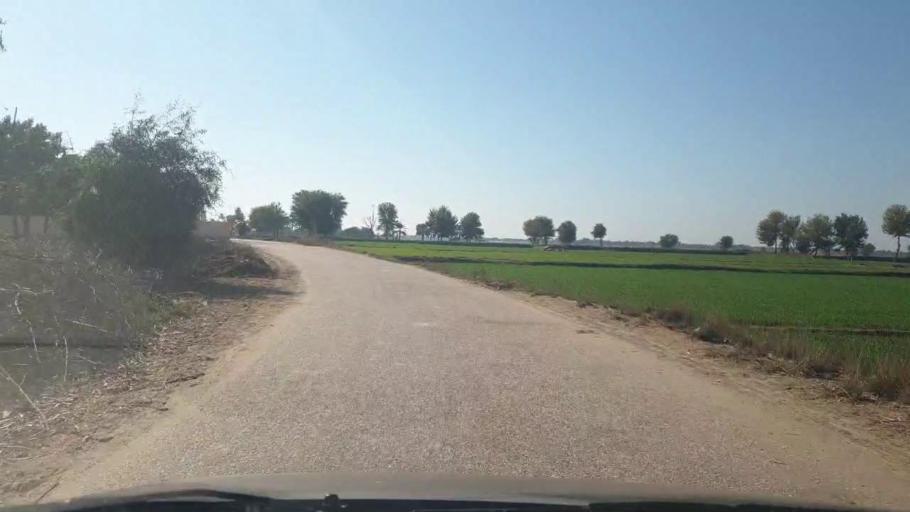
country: PK
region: Sindh
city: Bozdar
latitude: 27.1433
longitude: 68.6453
